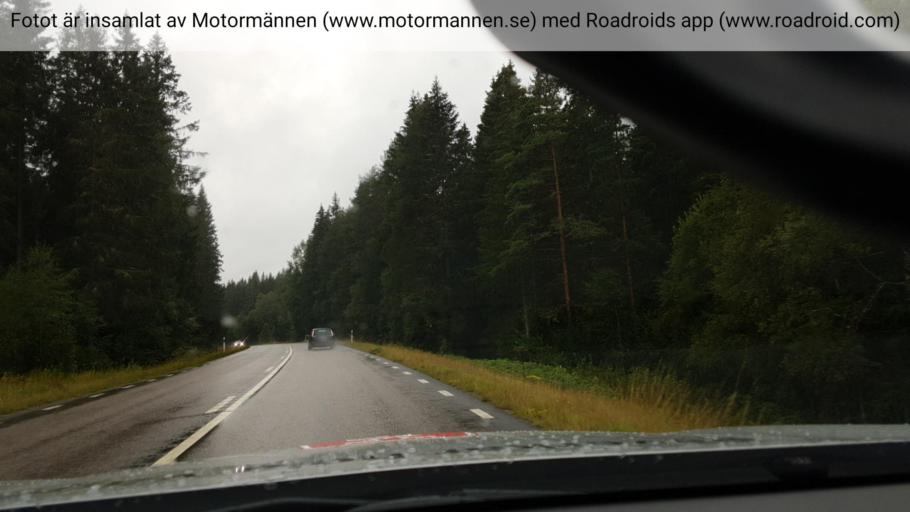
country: SE
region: Vaestra Goetaland
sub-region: Dals-Ed Kommun
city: Ed
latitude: 58.8861
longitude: 11.9099
